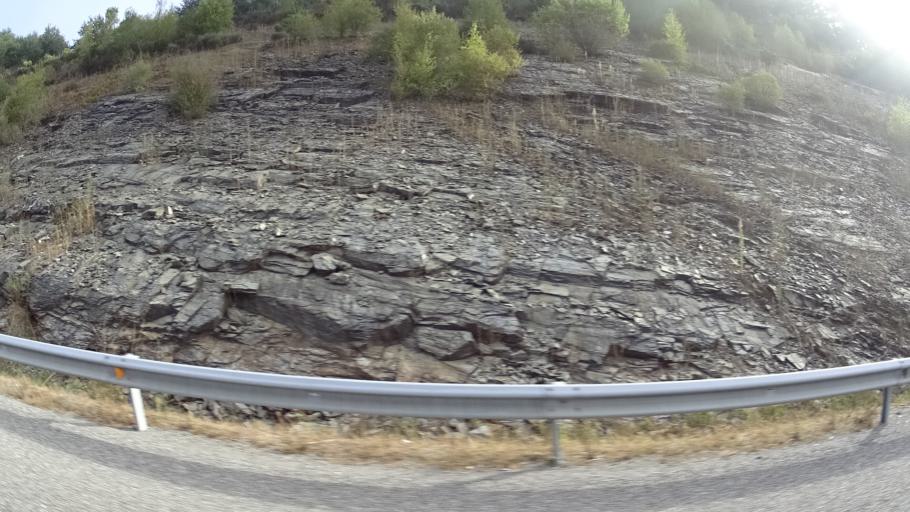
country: ES
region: Galicia
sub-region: Provincia de Lugo
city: Baralla
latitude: 42.9027
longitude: -7.2776
